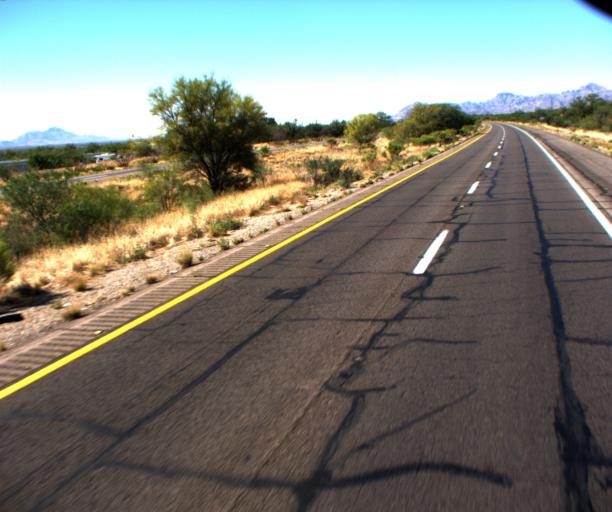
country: US
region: Arizona
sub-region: Pima County
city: Arivaca Junction
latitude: 31.7153
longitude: -111.0635
